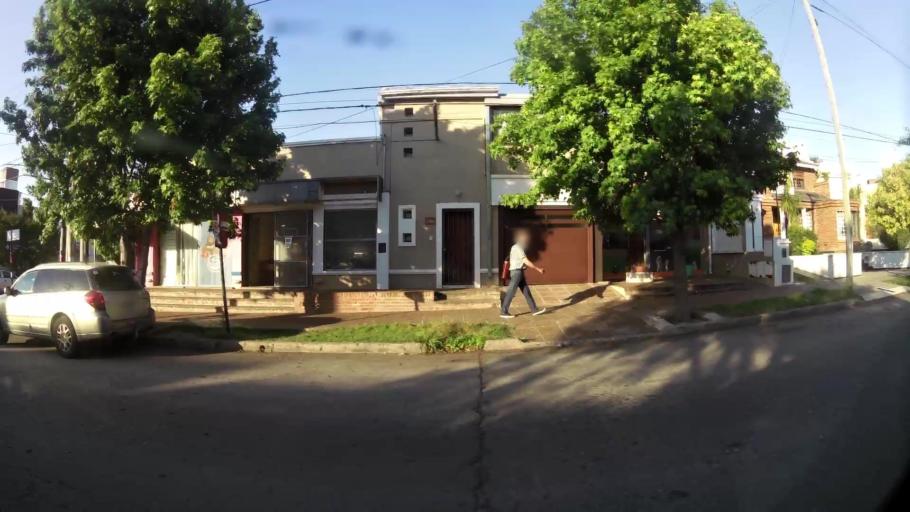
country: AR
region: Cordoba
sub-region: Departamento de Capital
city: Cordoba
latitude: -31.3843
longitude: -64.2393
